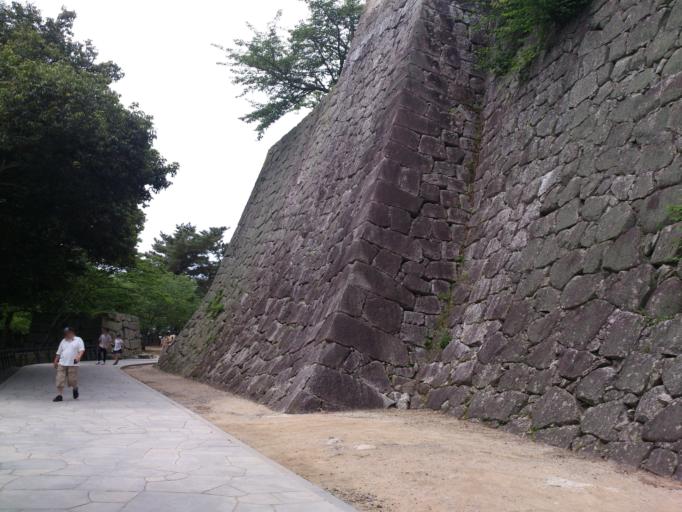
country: JP
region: Ehime
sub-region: Shikoku-chuo Shi
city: Matsuyama
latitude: 33.8438
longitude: 132.7672
